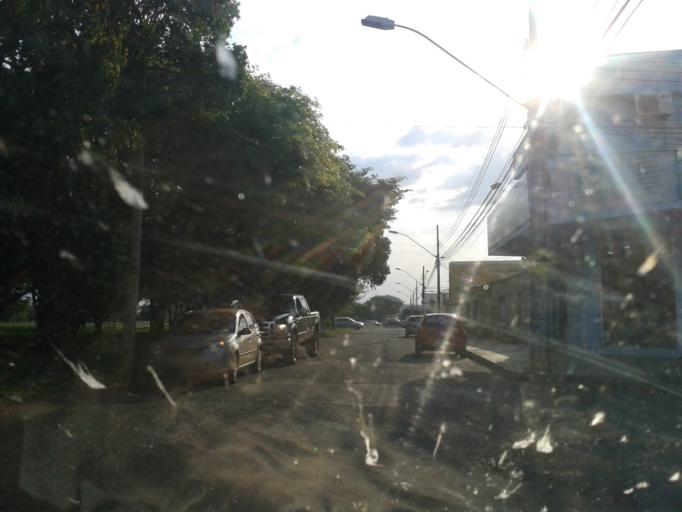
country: BR
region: Minas Gerais
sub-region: Uberlandia
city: Uberlandia
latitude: -18.9406
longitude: -48.3143
